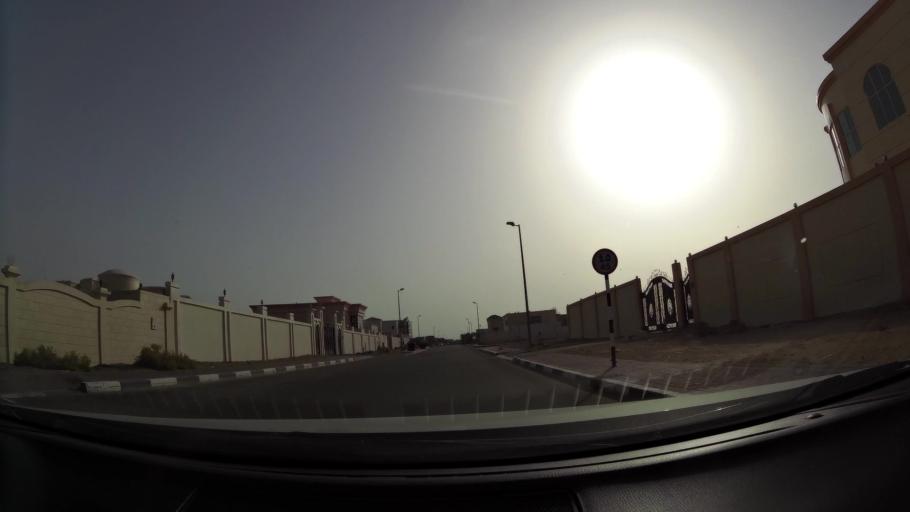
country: AE
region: Abu Dhabi
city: Al Ain
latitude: 24.1225
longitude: 55.6896
